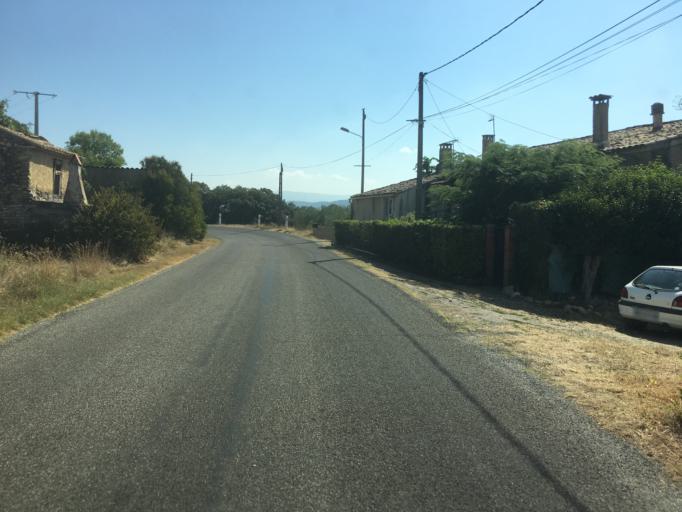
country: FR
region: Provence-Alpes-Cote d'Azur
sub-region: Departement des Alpes-de-Haute-Provence
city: Oraison
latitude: 43.8872
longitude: 5.9442
